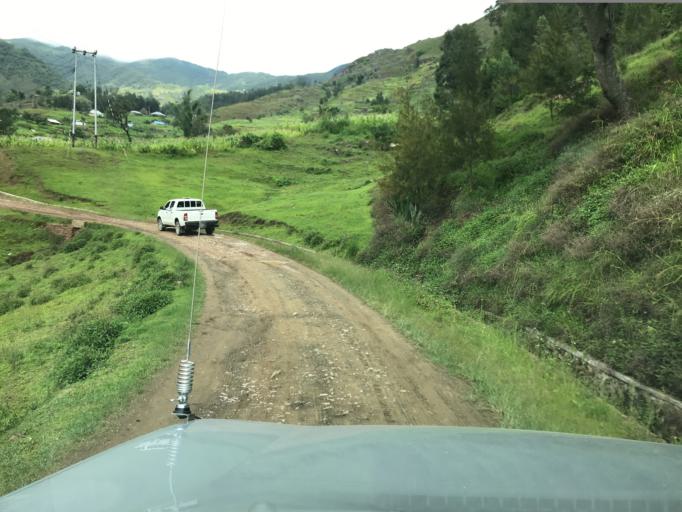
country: TL
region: Aileu
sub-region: Aileu Villa
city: Aileu
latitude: -8.8587
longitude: 125.5735
